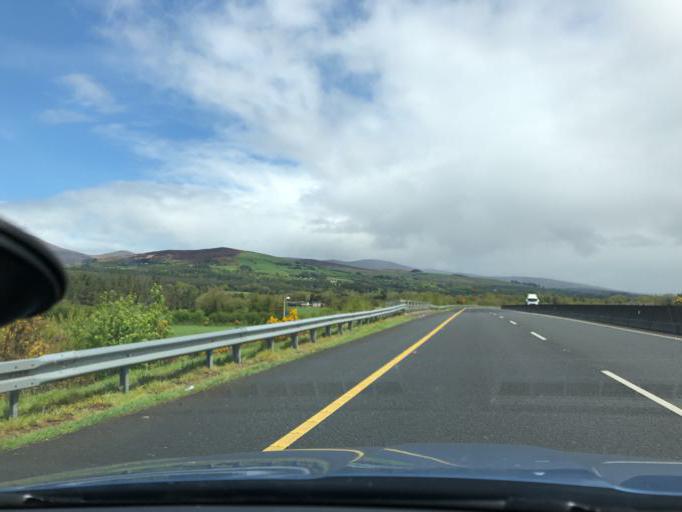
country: IE
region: Munster
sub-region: County Cork
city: Mitchelstown
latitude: 52.3015
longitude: -8.1734
